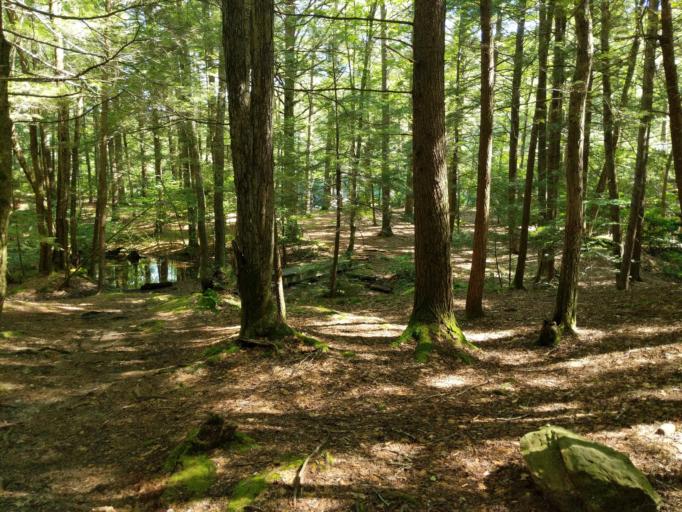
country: US
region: Massachusetts
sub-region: Hampden County
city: Holland
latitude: 42.0058
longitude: -72.1296
